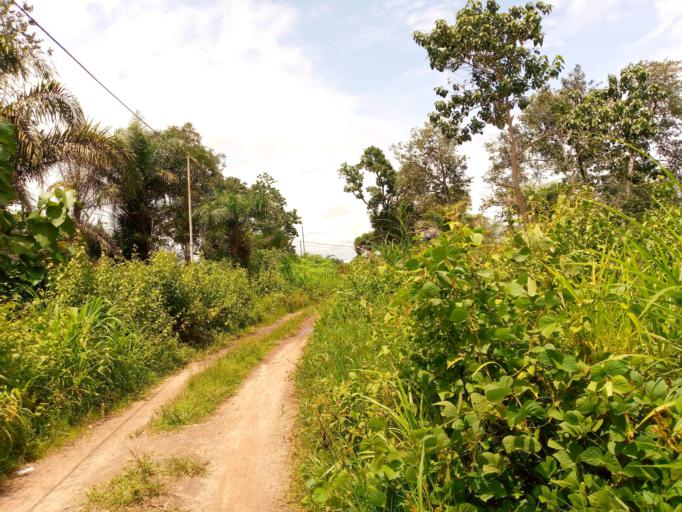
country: SL
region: Northern Province
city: Magburaka
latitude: 8.7263
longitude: -11.9266
